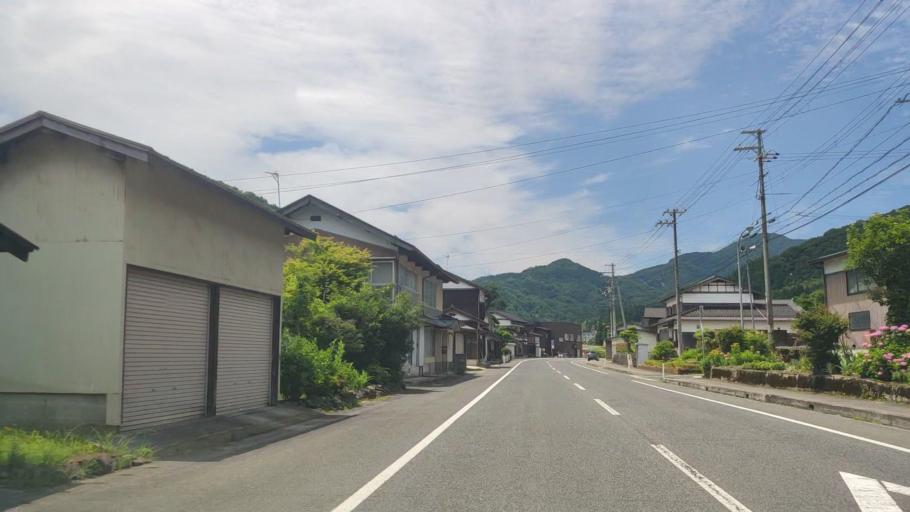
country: JP
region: Hyogo
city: Toyooka
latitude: 35.4636
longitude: 134.5437
